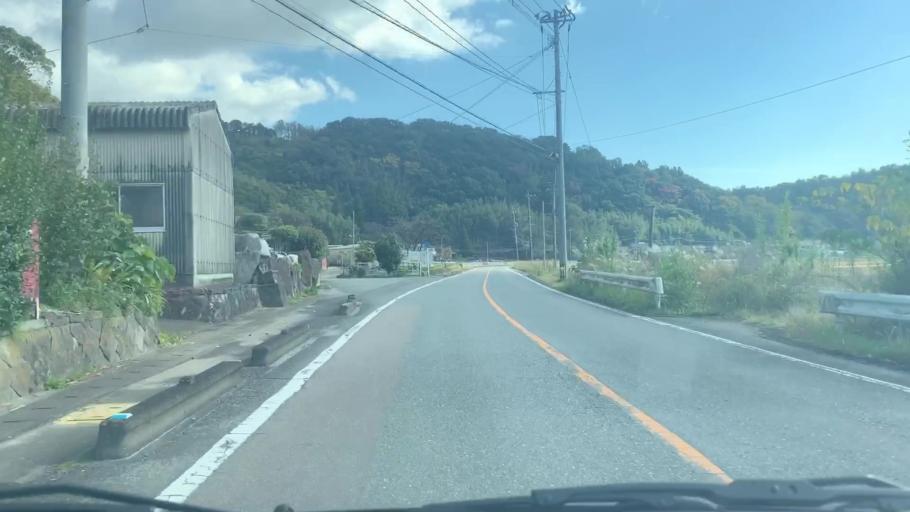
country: JP
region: Saga Prefecture
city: Saga-shi
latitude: 33.2752
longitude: 130.1718
